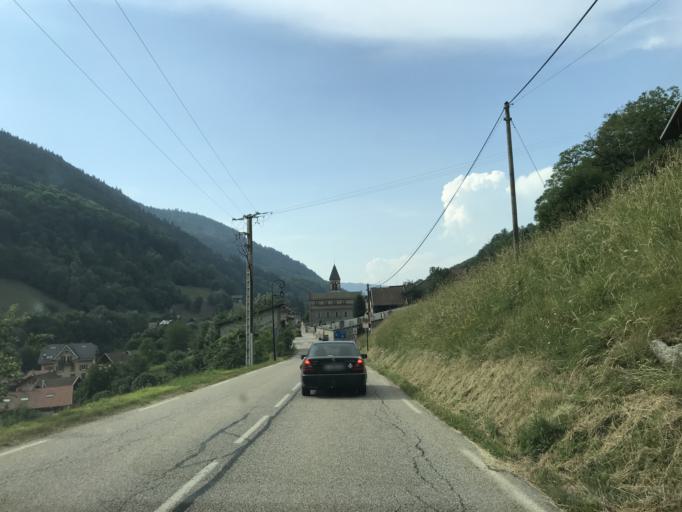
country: FR
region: Rhone-Alpes
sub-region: Departement de l'Isere
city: Allevard
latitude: 45.3554
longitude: 6.1010
